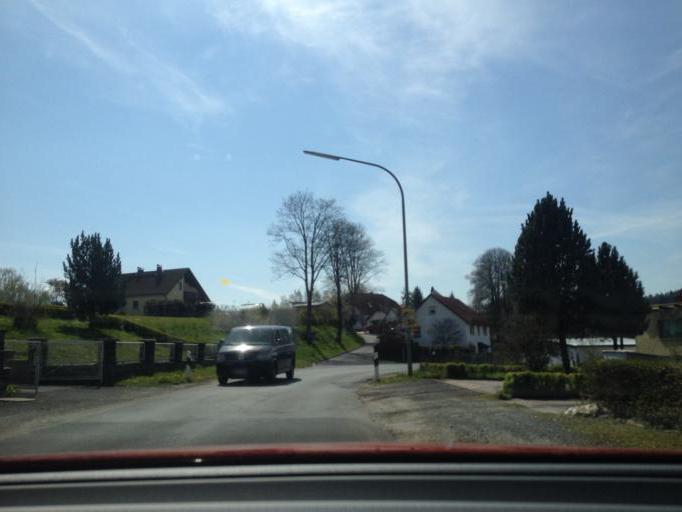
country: DE
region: Bavaria
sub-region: Upper Franconia
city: Thiersheim
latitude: 50.0740
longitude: 12.1314
